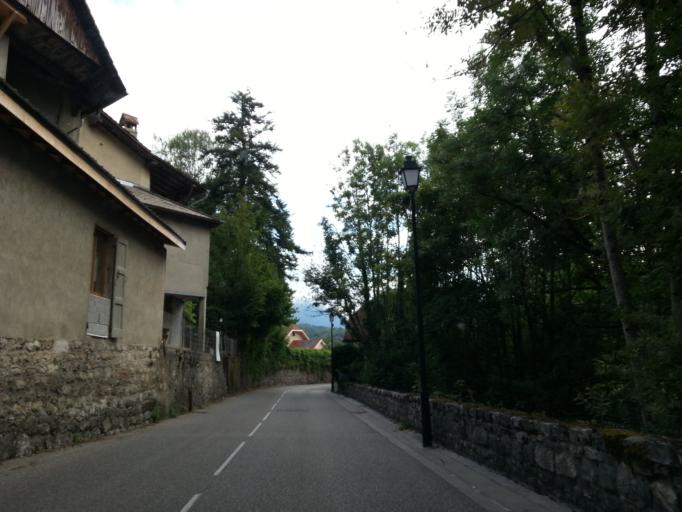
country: FR
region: Rhone-Alpes
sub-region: Departement de la Haute-Savoie
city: Menthon-Saint-Bernard
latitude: 45.8633
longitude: 6.1998
